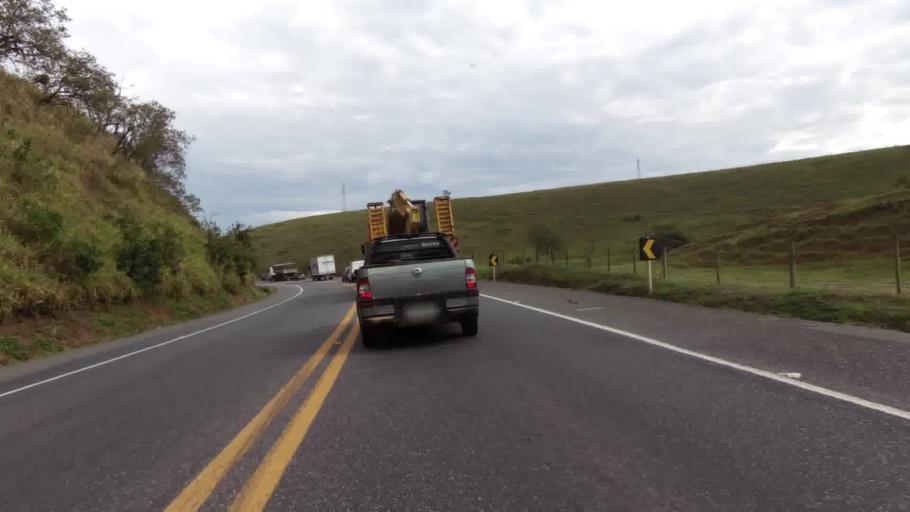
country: BR
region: Espirito Santo
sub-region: Alfredo Chaves
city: Alfredo Chaves
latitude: -20.6897
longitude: -40.6947
